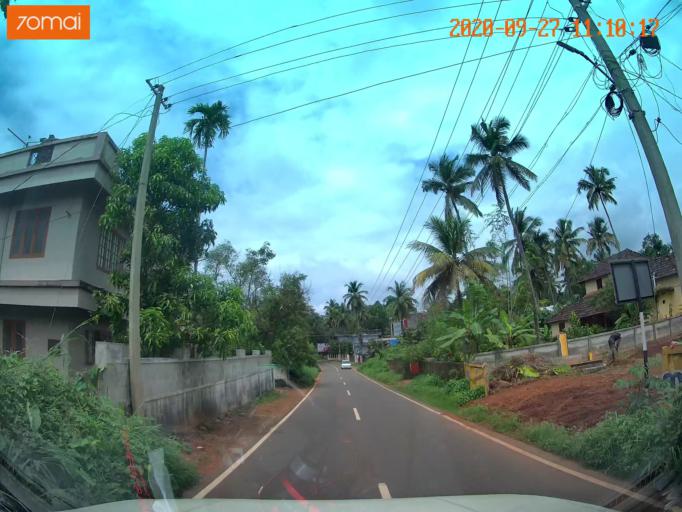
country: IN
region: Kerala
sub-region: Thrissur District
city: Trichur
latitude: 10.4305
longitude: 76.2211
